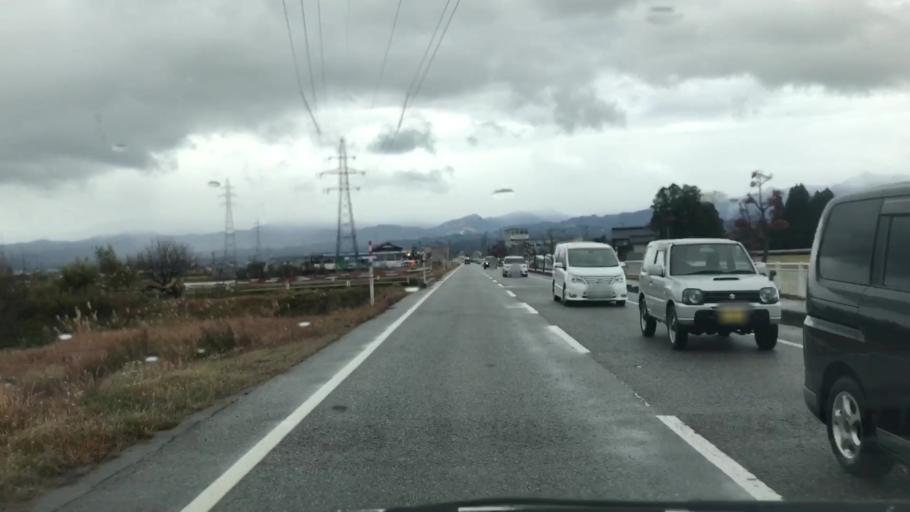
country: JP
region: Toyama
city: Kamiichi
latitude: 36.6866
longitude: 137.3055
